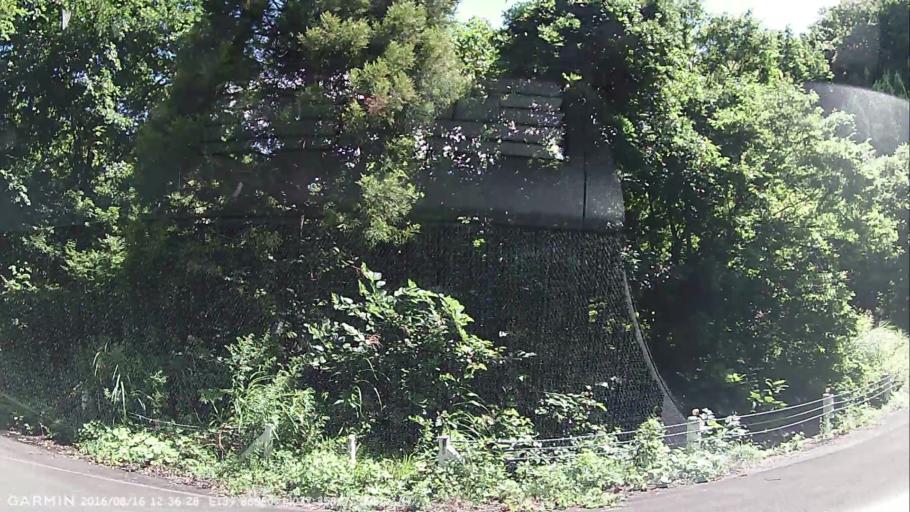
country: JP
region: Fukushima
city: Kitakata
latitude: 37.3582
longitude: 139.8666
